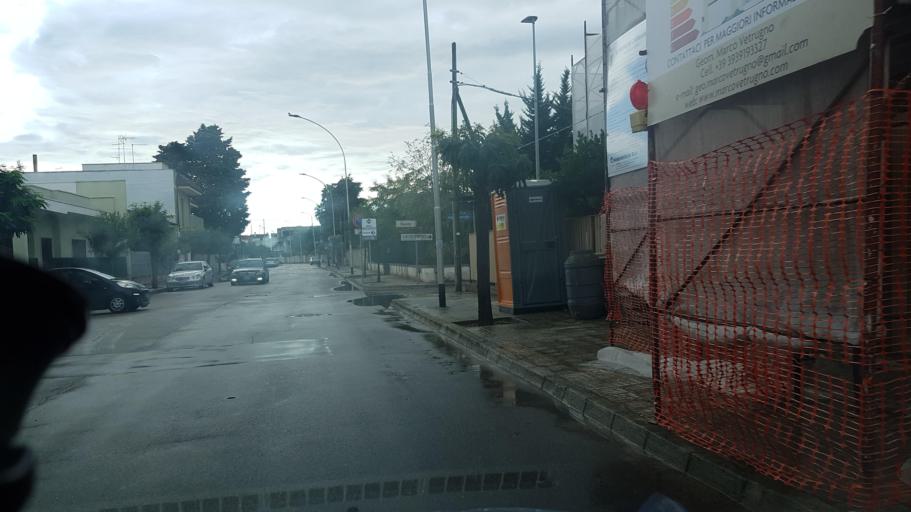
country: IT
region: Apulia
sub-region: Provincia di Lecce
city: Carmiano
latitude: 40.3432
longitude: 18.0481
